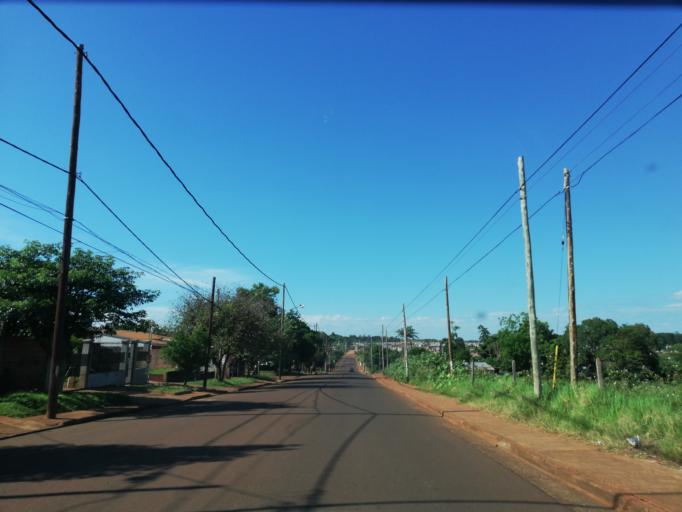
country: AR
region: Misiones
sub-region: Departamento de Capital
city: Posadas
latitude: -27.4246
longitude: -55.9506
